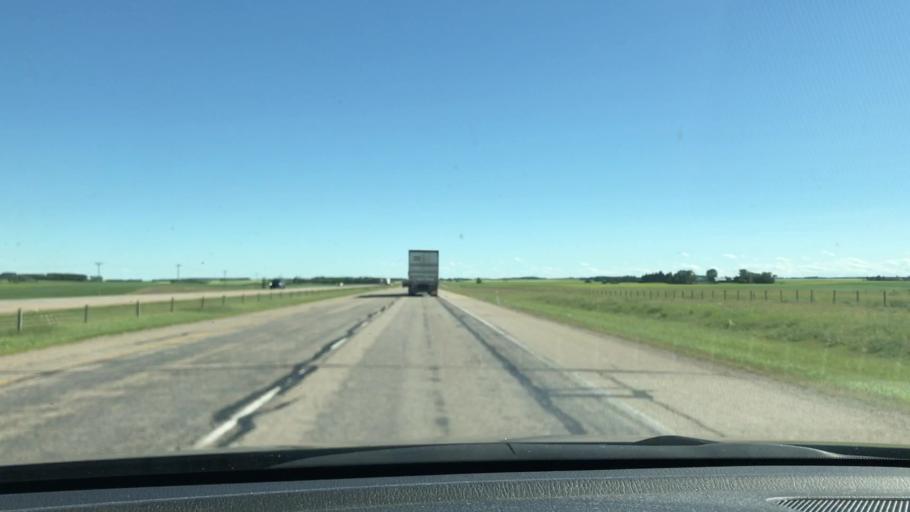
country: CA
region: Alberta
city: Olds
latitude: 51.8778
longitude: -114.0256
